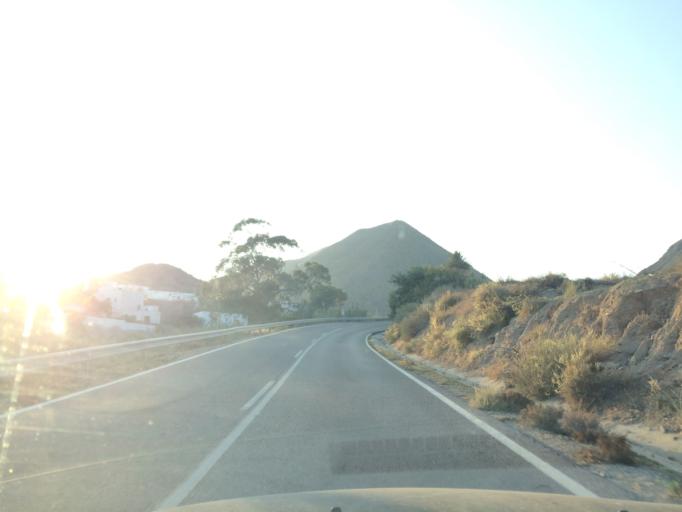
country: ES
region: Andalusia
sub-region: Provincia de Almeria
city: San Jose
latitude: 36.8746
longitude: -2.0305
